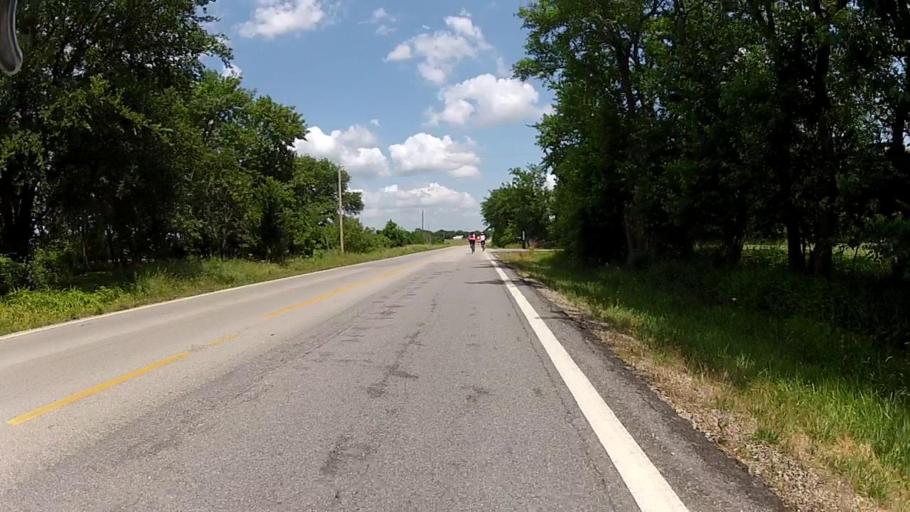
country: US
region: Kansas
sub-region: Labette County
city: Altamont
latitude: 37.1931
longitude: -95.3250
